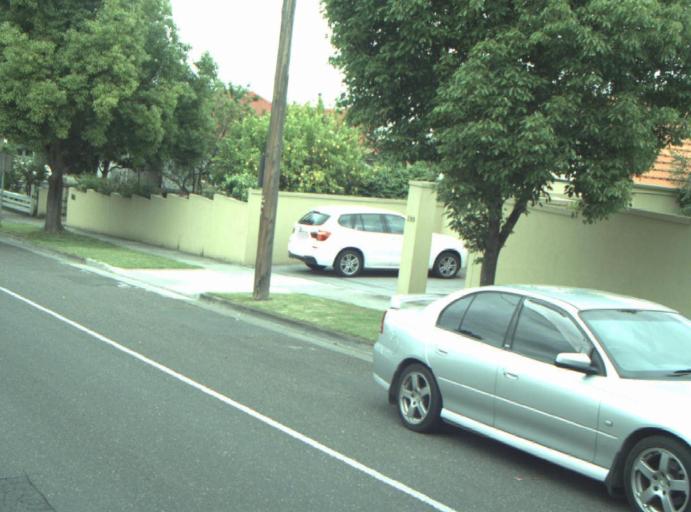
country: AU
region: Victoria
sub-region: Greater Geelong
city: Geelong West
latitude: -38.1533
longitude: 144.3459
